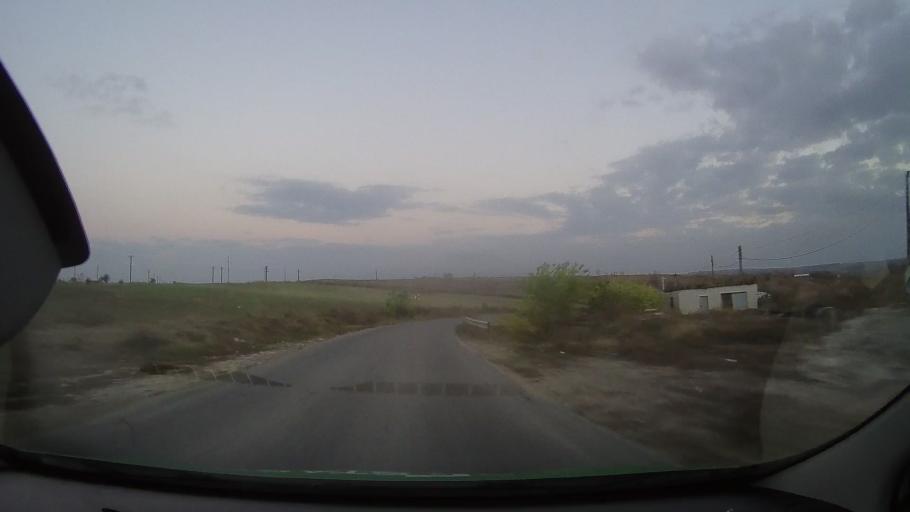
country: RO
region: Constanta
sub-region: Comuna Baneasa
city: Baneasa
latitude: 44.0782
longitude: 27.6953
